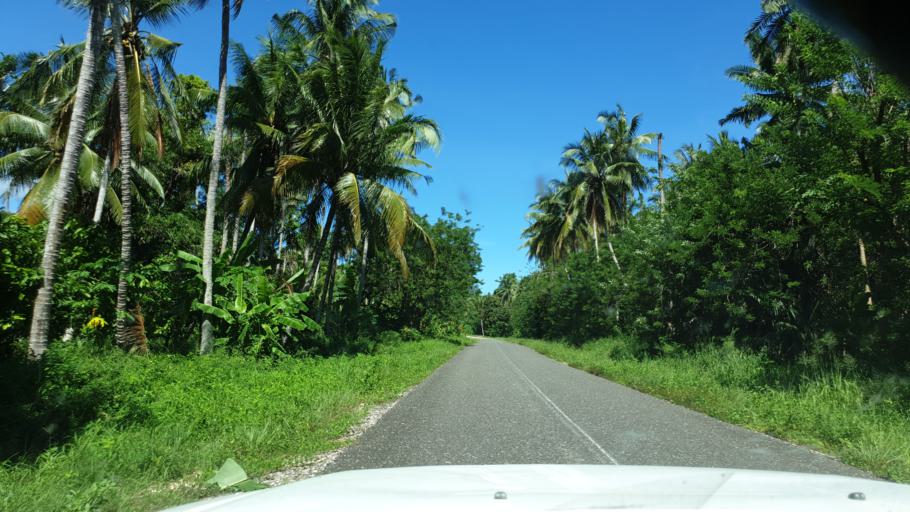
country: PG
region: Madang
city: Madang
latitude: -4.4930
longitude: 145.4500
